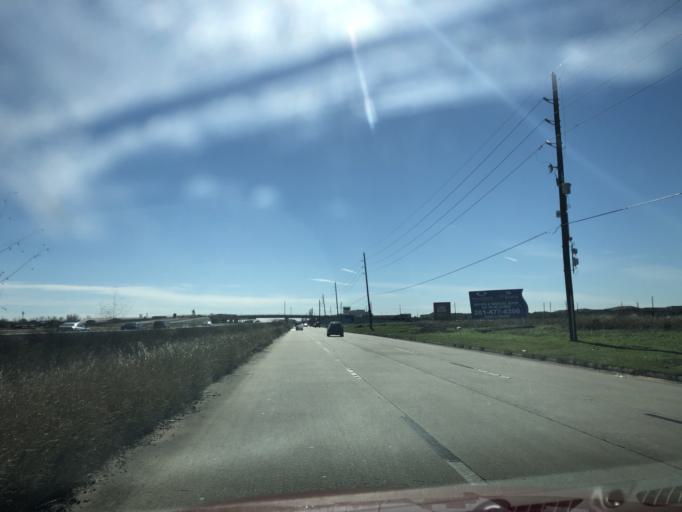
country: US
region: Texas
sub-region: Brazoria County
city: Brookside Village
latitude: 29.5748
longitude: -95.3865
